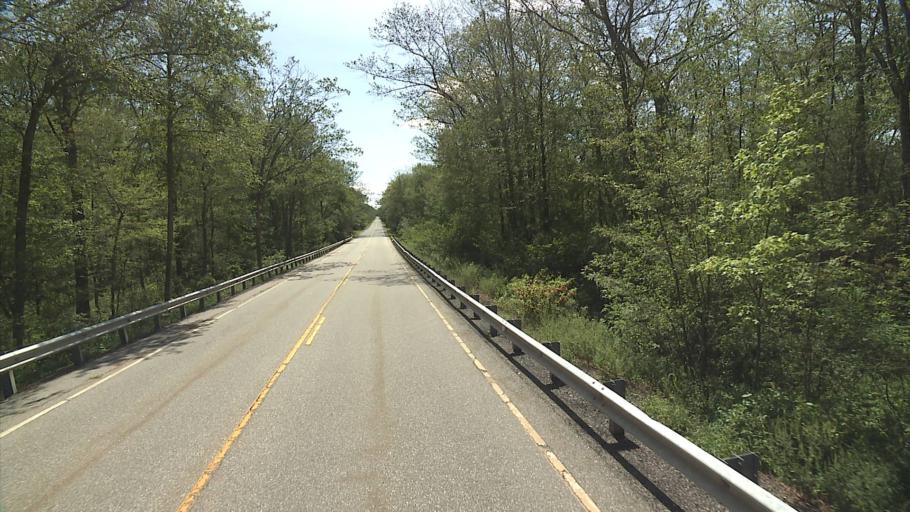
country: US
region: Rhode Island
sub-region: Washington County
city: Hope Valley
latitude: 41.5538
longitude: -71.7919
